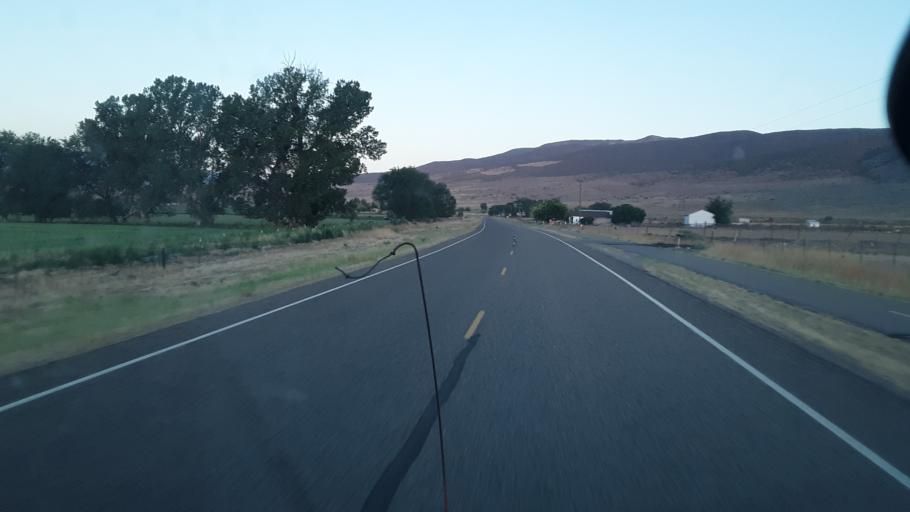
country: US
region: Utah
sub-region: Sevier County
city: Monroe
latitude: 38.6530
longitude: -112.2019
